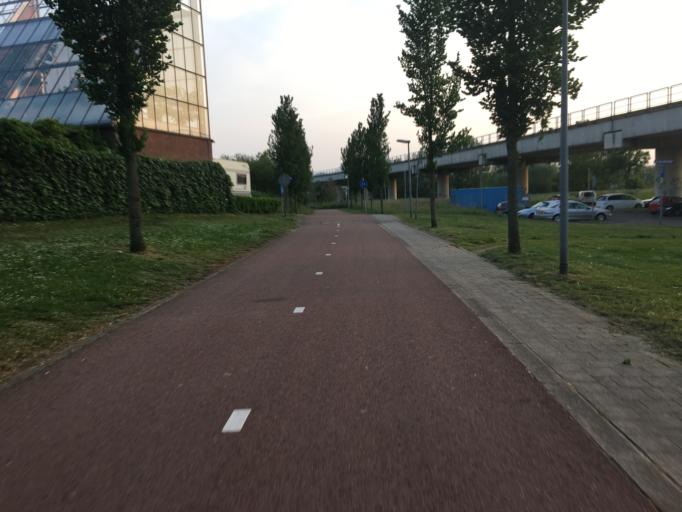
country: NL
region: South Holland
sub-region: Gemeente Schiedam
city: Schiedam
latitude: 51.9119
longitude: 4.3748
